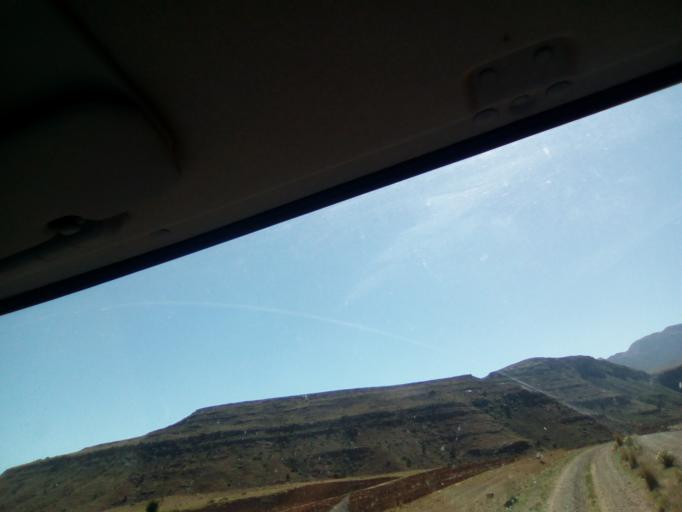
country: LS
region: Qacha's Nek
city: Qacha's Nek
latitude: -30.0590
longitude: 28.6289
